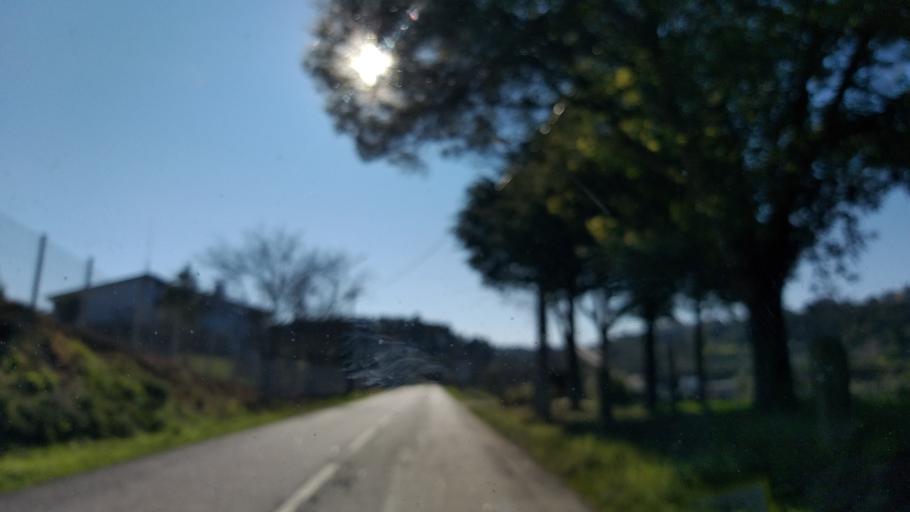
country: PT
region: Guarda
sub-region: Celorico da Beira
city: Celorico da Beira
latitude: 40.6307
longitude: -7.3862
